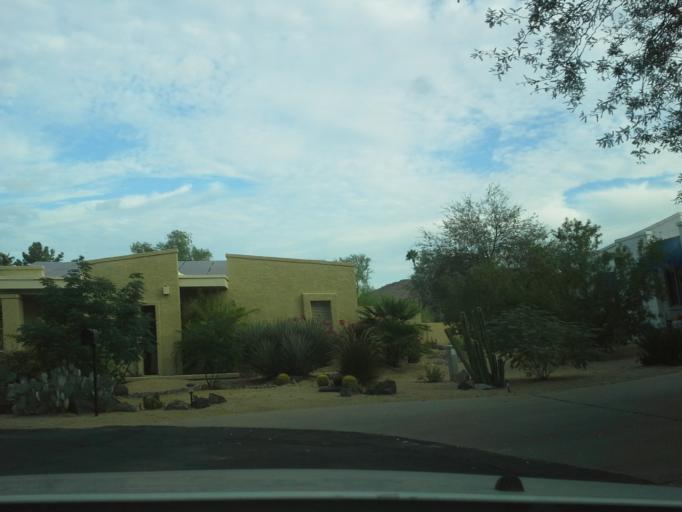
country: US
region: Arizona
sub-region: Maricopa County
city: Paradise Valley
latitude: 33.6081
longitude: -112.0573
